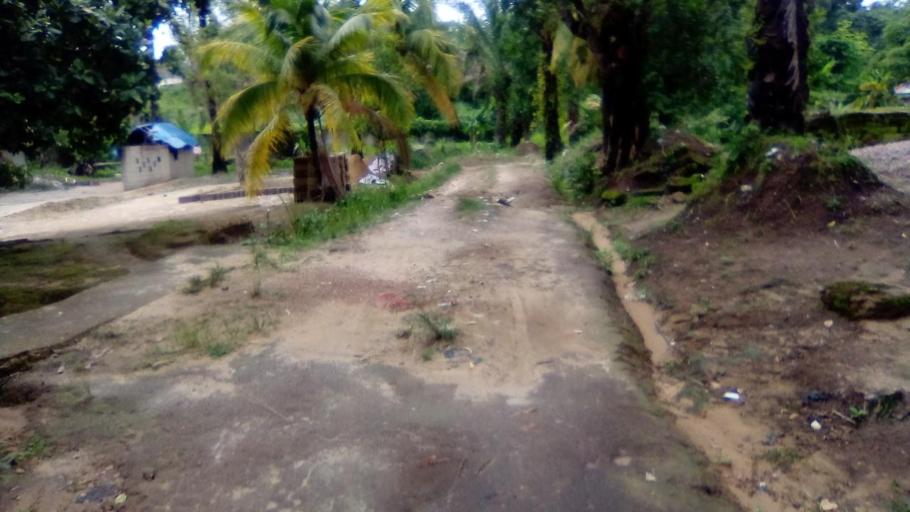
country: SL
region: Southern Province
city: Bo
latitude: 7.9500
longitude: -11.7505
